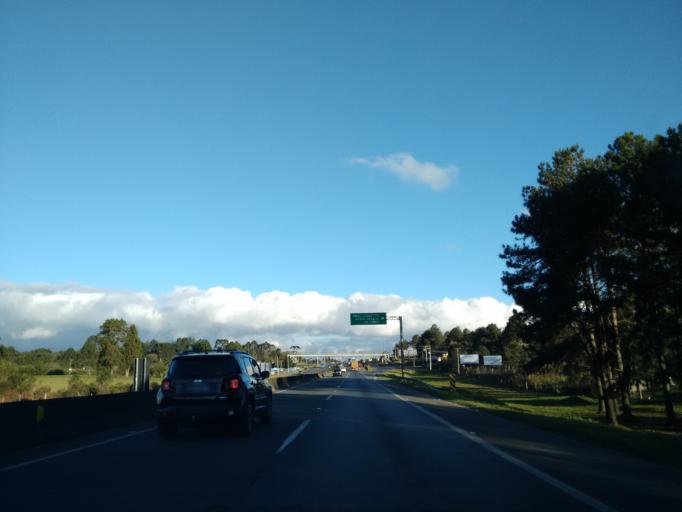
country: BR
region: Parana
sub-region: Sao Jose Dos Pinhais
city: Sao Jose dos Pinhais
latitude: -25.6603
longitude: -49.1552
